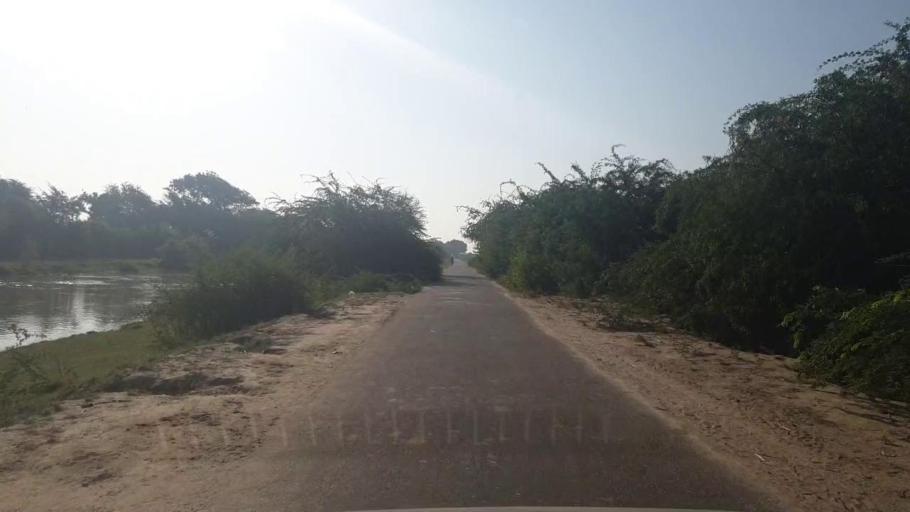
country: PK
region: Sindh
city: Tando Bago
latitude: 24.7240
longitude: 68.9387
